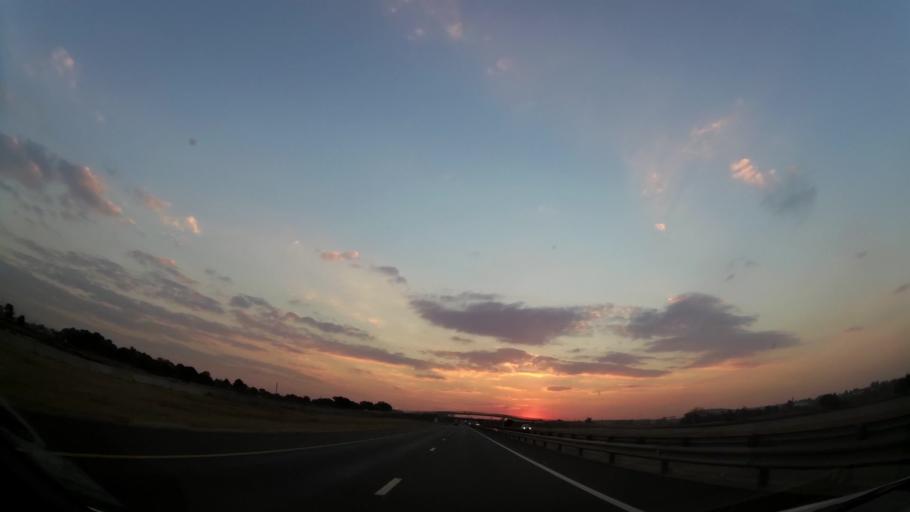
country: ZA
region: Gauteng
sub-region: Ekurhuleni Metropolitan Municipality
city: Springs
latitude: -26.2806
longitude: 28.4102
